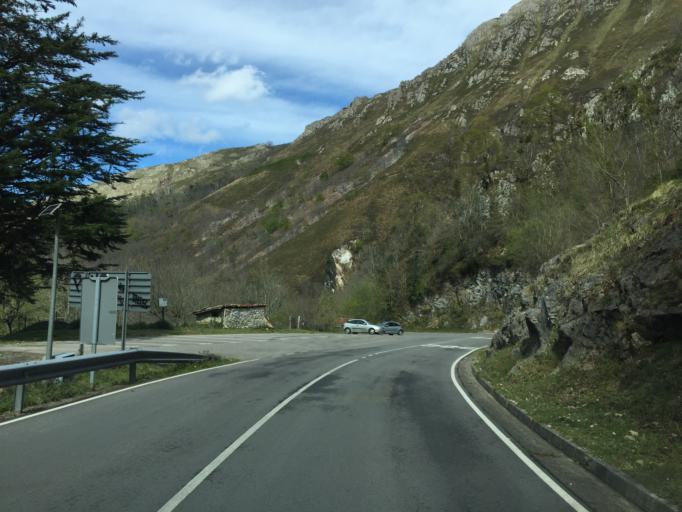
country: ES
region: Asturias
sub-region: Province of Asturias
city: Amieva
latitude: 43.3072
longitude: -5.0505
